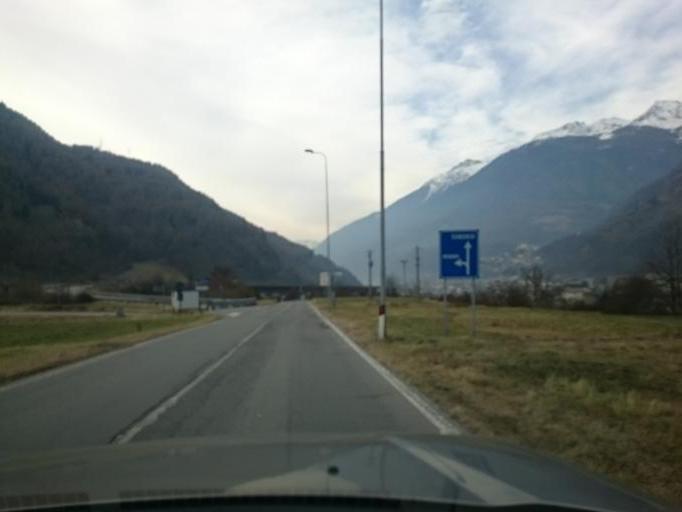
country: IT
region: Lombardy
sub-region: Provincia di Sondrio
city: Grosio
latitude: 46.3071
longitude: 10.2939
